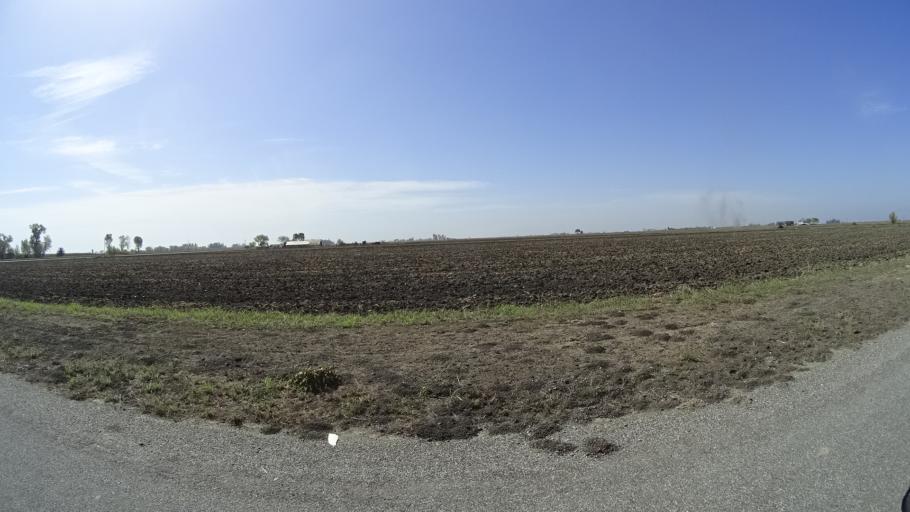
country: US
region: California
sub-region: Glenn County
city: Hamilton City
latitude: 39.6162
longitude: -122.0673
